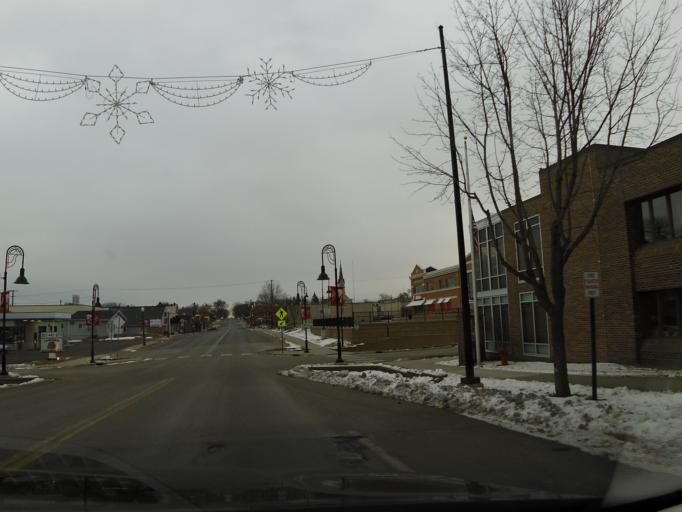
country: US
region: Minnesota
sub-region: Carver County
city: Waconia
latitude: 44.8505
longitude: -93.7911
